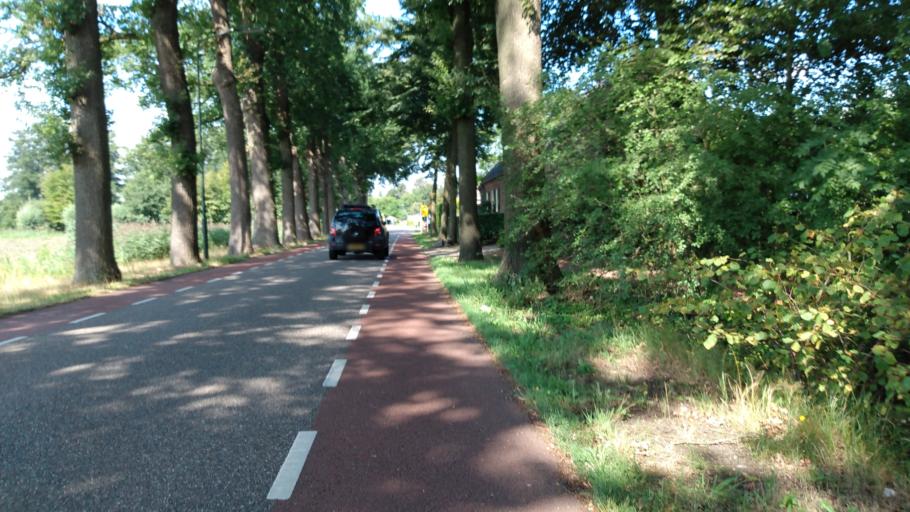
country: NL
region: North Brabant
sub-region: Gemeente Oisterwijk
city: Oisterwijk
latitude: 51.5451
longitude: 5.1899
